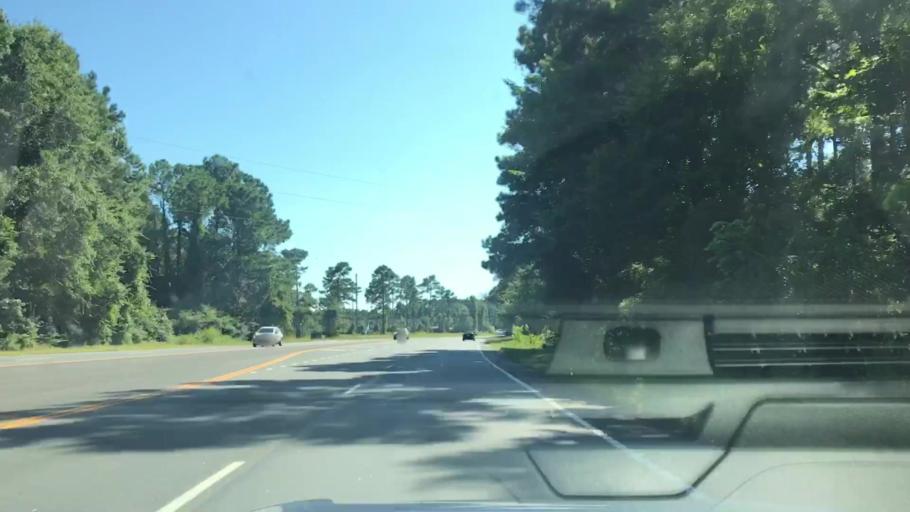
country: US
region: South Carolina
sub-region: Charleston County
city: Awendaw
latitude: 33.1011
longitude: -79.4680
